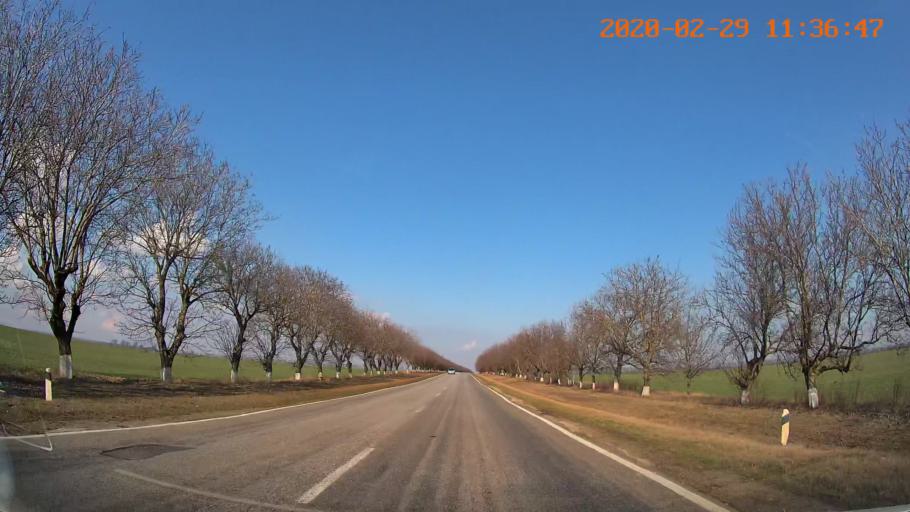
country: MD
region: Rezina
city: Saharna
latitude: 47.6015
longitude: 29.0522
